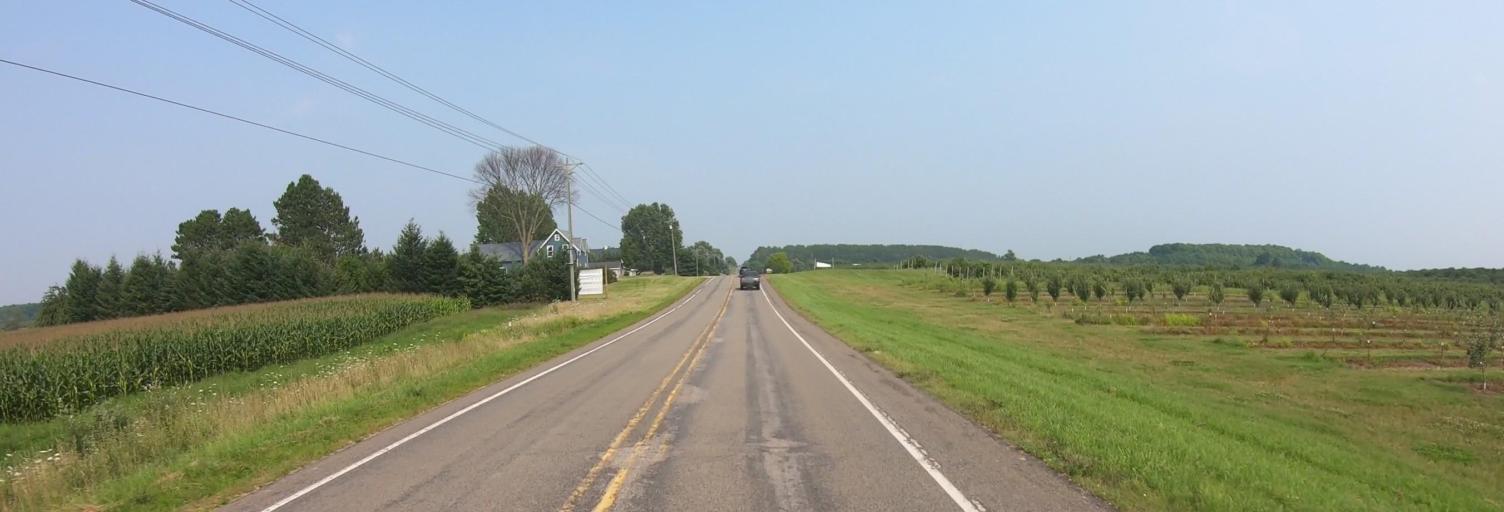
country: US
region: Michigan
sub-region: Charlevoix County
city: Charlevoix
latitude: 45.1860
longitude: -85.3379
